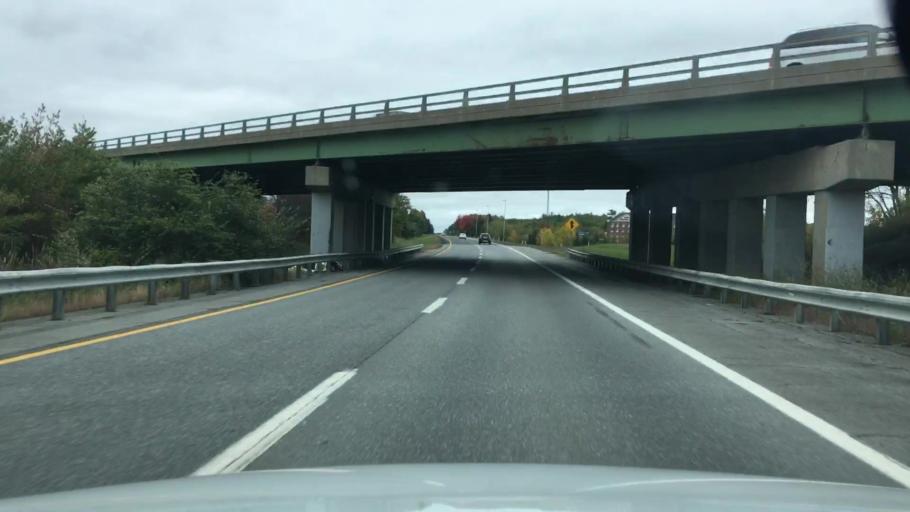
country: US
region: Maine
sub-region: Penobscot County
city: Veazie
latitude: 44.8318
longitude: -68.7418
